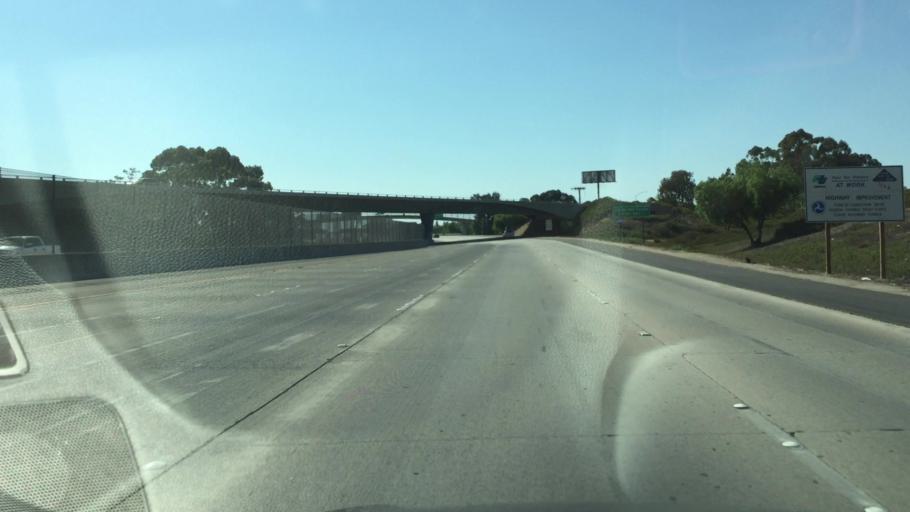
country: MX
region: Baja California
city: Tijuana
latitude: 32.5487
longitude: -117.0388
